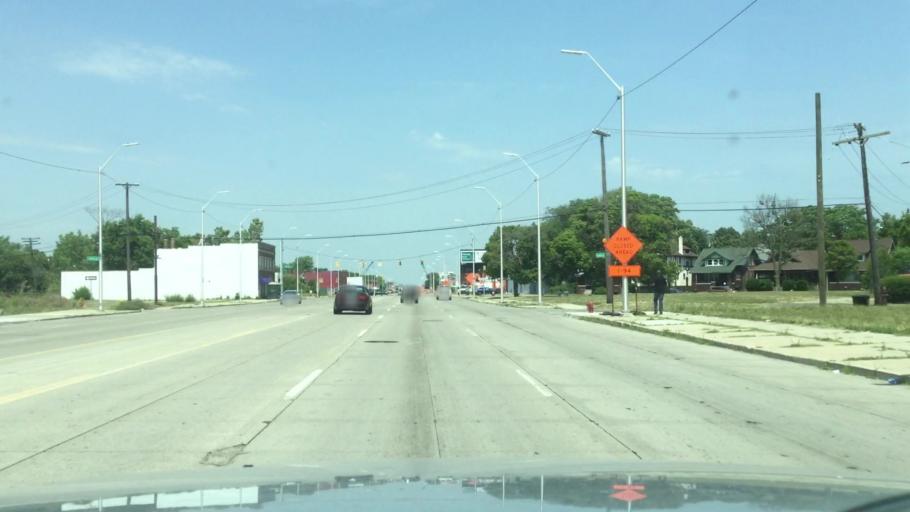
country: US
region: Michigan
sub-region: Wayne County
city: Hamtramck
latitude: 42.3829
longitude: -83.0119
